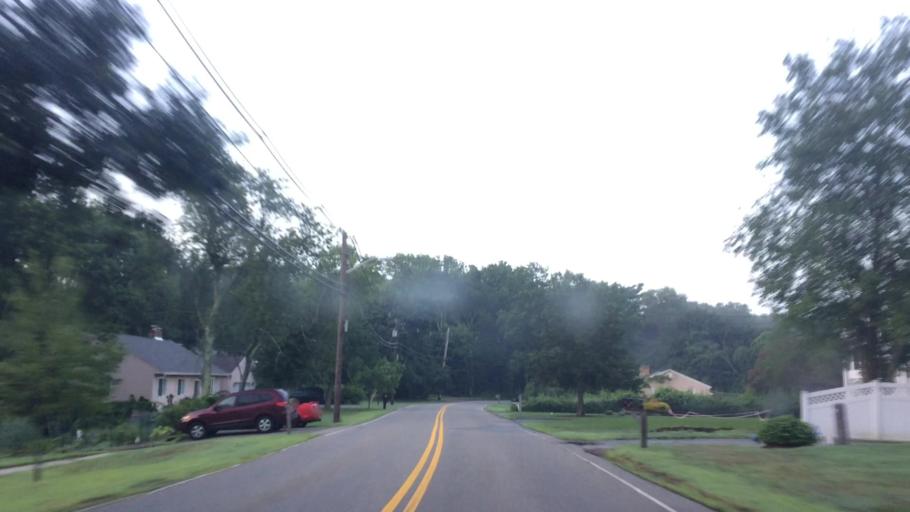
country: US
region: Massachusetts
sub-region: Essex County
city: Andover
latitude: 42.6429
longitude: -71.0875
